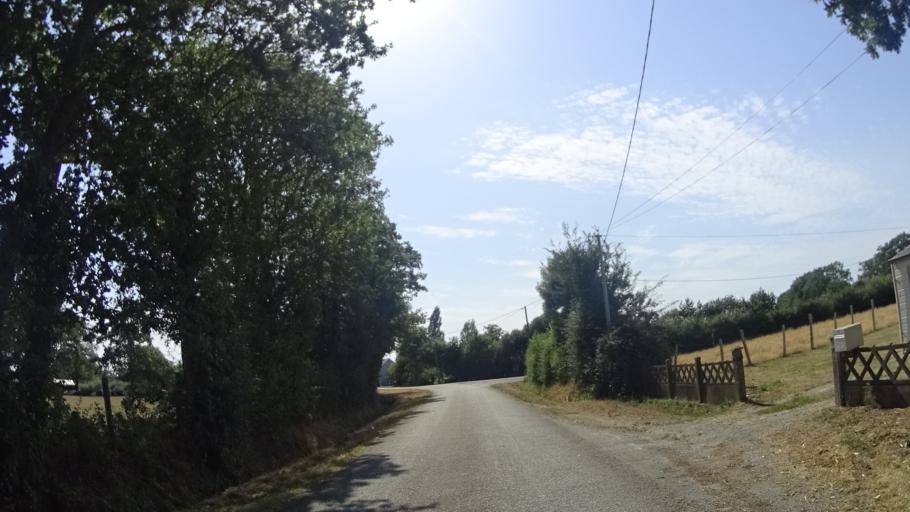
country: FR
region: Pays de la Loire
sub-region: Departement de la Loire-Atlantique
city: Prinquiau
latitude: 47.3399
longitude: -2.0176
